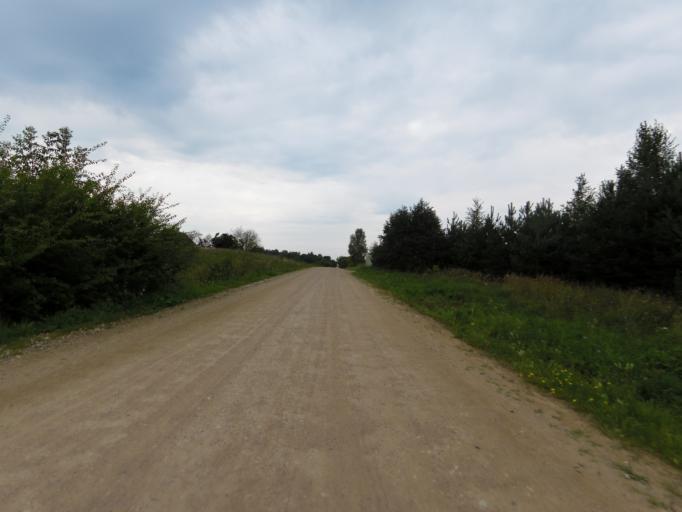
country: LT
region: Vilnius County
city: Pilaite
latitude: 54.7020
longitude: 25.1326
